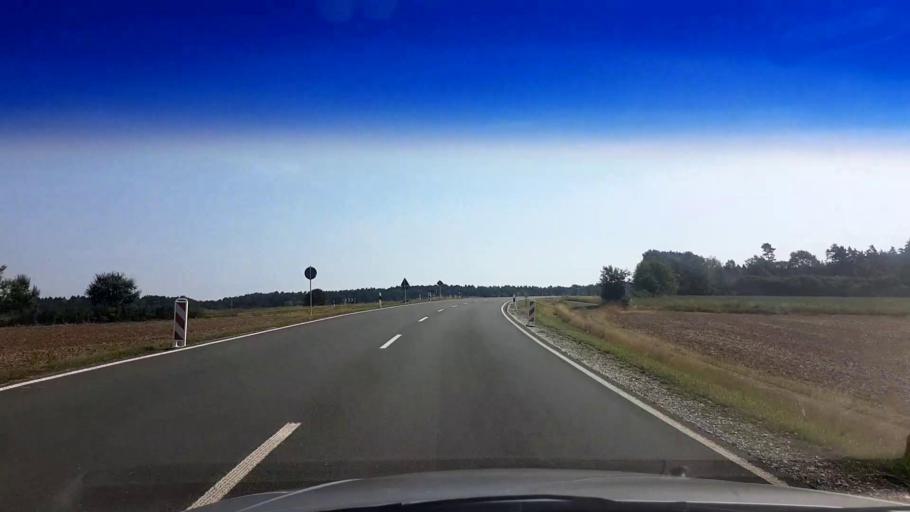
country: DE
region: Bavaria
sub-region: Upper Franconia
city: Hollfeld
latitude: 49.9433
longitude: 11.3062
